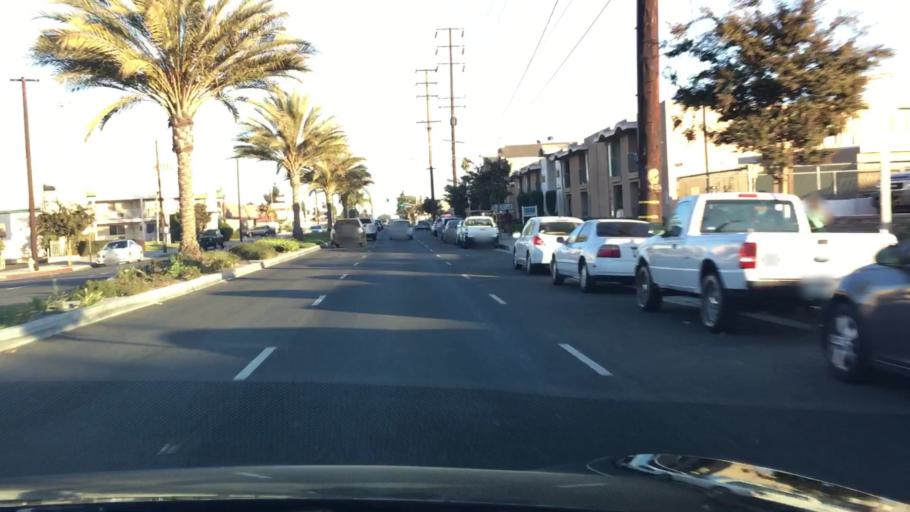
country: US
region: California
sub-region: Los Angeles County
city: Santa Fe Springs
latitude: 33.9570
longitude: -118.1044
